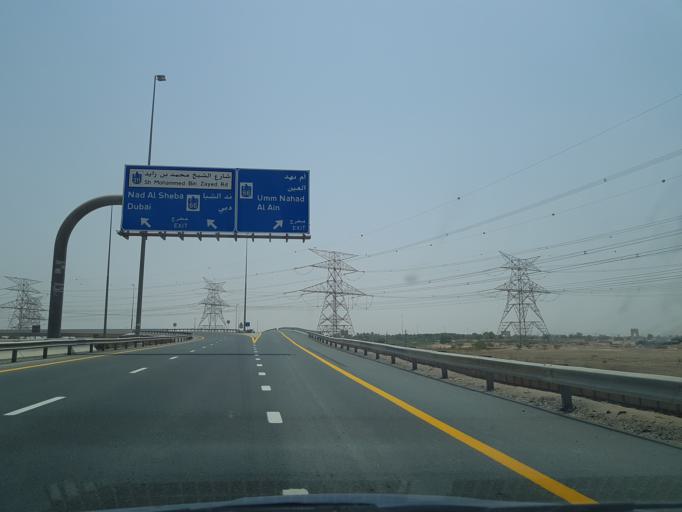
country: AE
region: Dubai
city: Dubai
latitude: 25.0848
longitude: 55.3911
